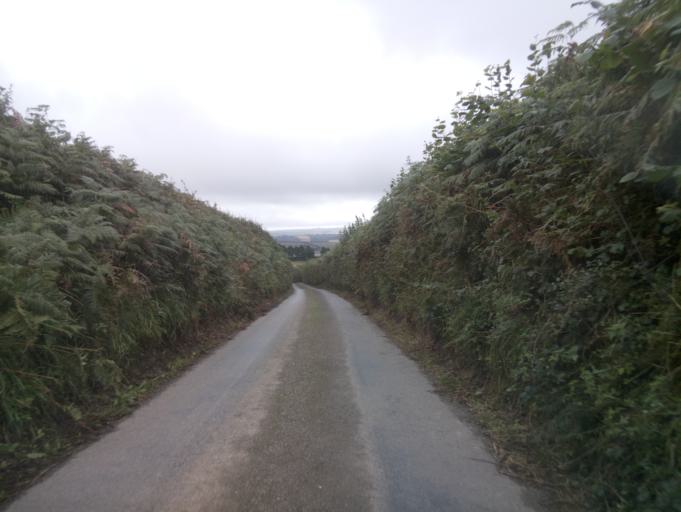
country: GB
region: England
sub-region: Devon
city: Kingsbridge
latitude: 50.2990
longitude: -3.7169
